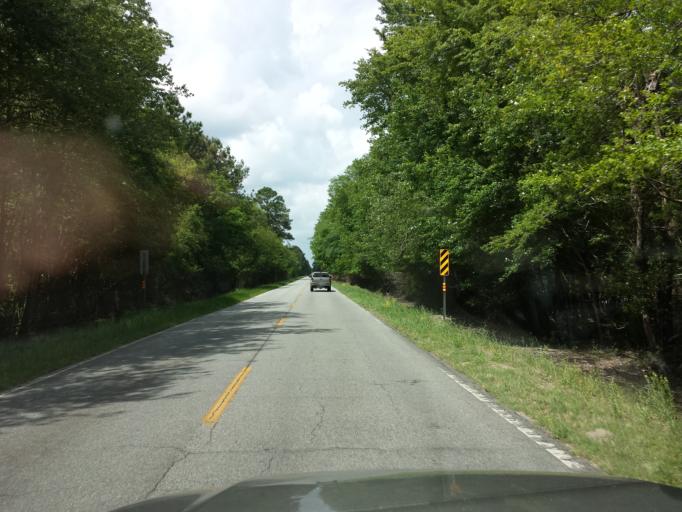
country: US
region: Georgia
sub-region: Echols County
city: Statenville
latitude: 30.6670
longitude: -83.1617
